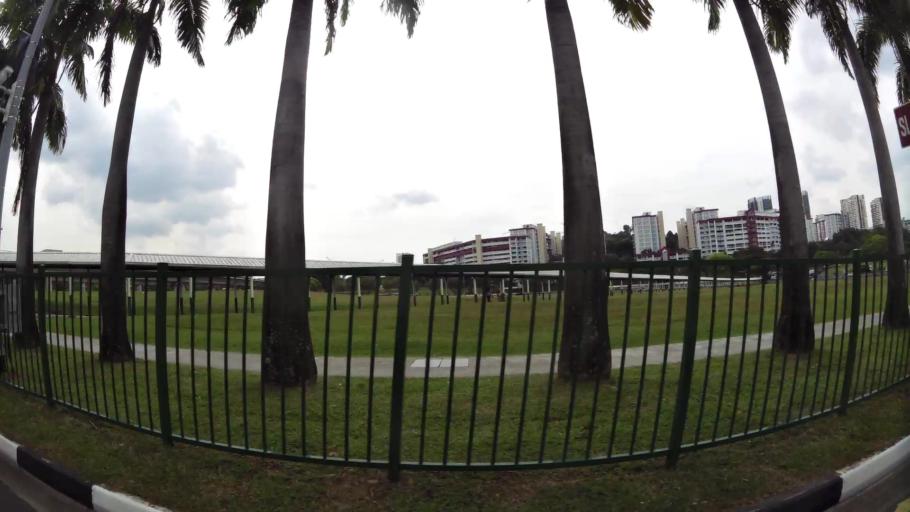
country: MY
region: Johor
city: Johor Bahru
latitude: 1.4372
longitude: 103.7846
